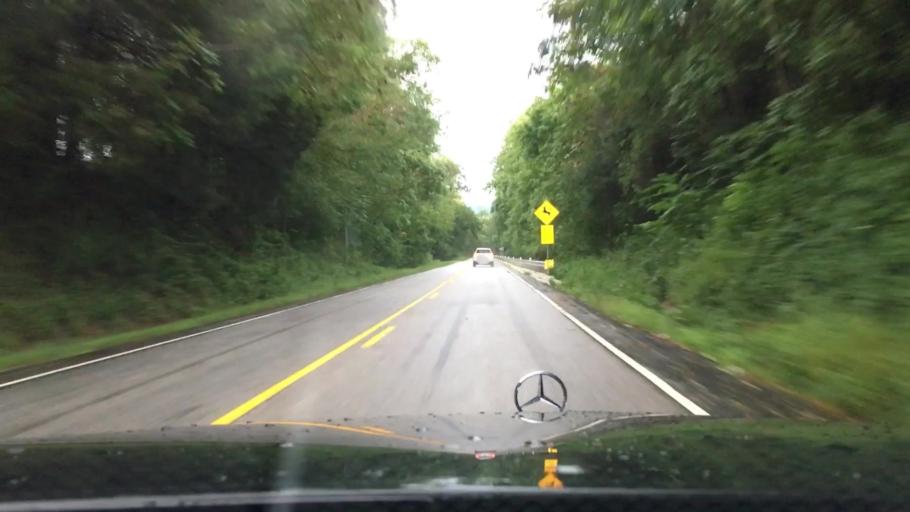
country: US
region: Virginia
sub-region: Amherst County
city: Amherst
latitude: 37.6782
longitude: -79.0198
